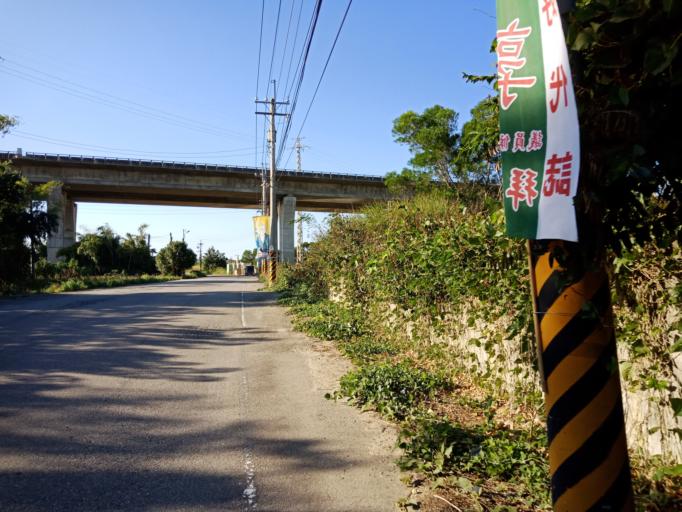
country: TW
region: Taiwan
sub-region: Miaoli
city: Miaoli
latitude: 24.4852
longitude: 120.7027
